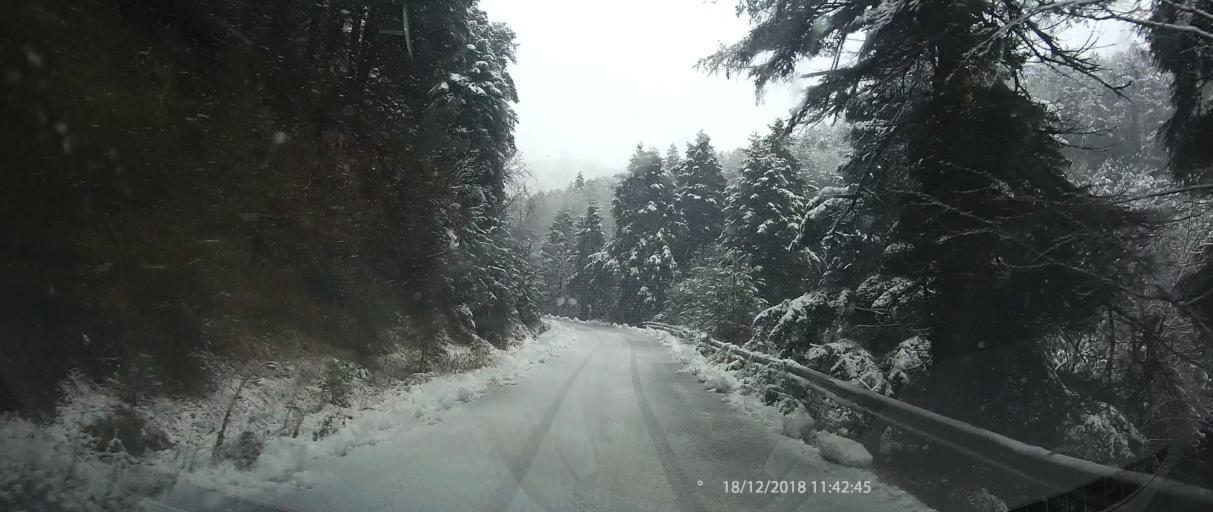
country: GR
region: Central Macedonia
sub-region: Nomos Pierias
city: Litochoro
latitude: 40.1098
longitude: 22.4712
